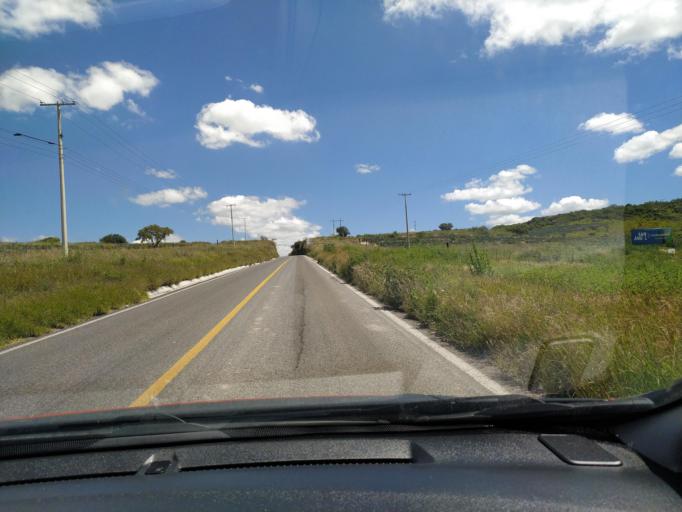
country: MX
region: Guanajuato
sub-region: Purisima del Rincon
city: Monte Grande
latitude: 21.0276
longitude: -101.9297
